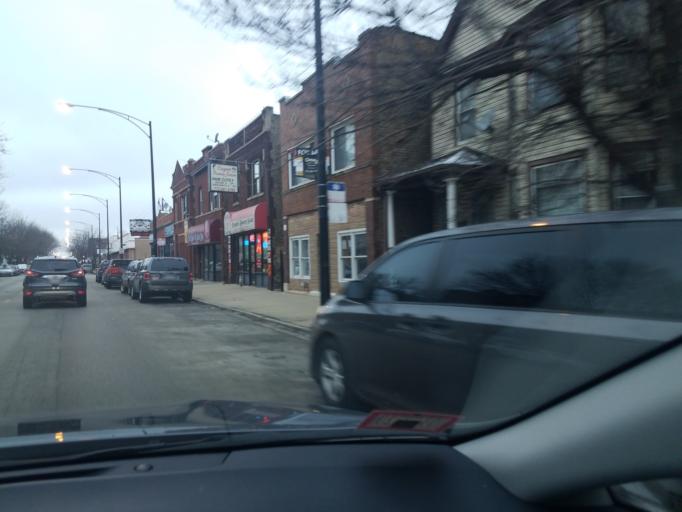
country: US
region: Illinois
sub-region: Cook County
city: Lincolnwood
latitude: 41.9611
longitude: -87.7233
